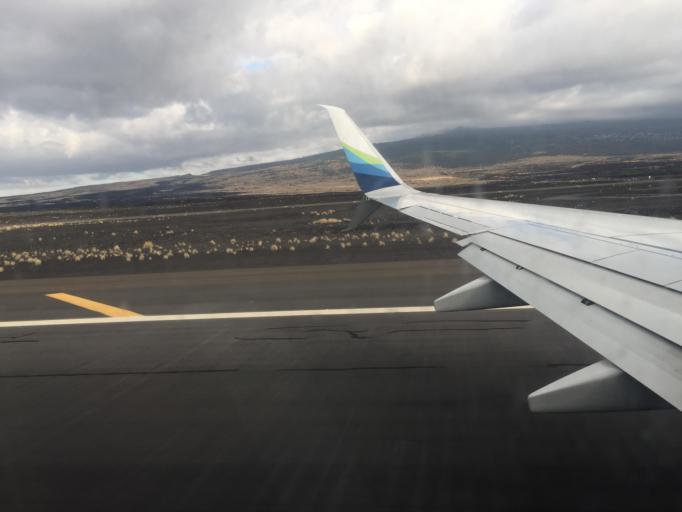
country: US
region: Hawaii
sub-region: Hawaii County
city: Kalaoa
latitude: 19.7519
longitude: -156.0445
